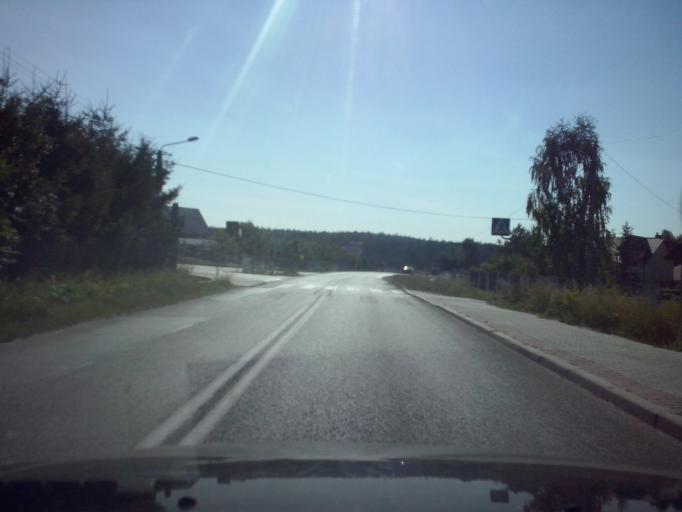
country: PL
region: Swietokrzyskie
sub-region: Powiat kielecki
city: Daleszyce
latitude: 50.8077
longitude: 20.7682
